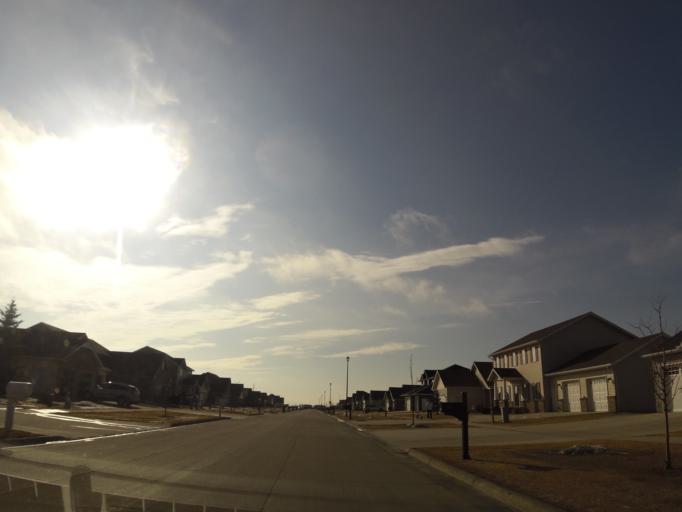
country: US
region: North Dakota
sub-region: Grand Forks County
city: Grand Forks
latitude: 47.8787
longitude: -97.0588
